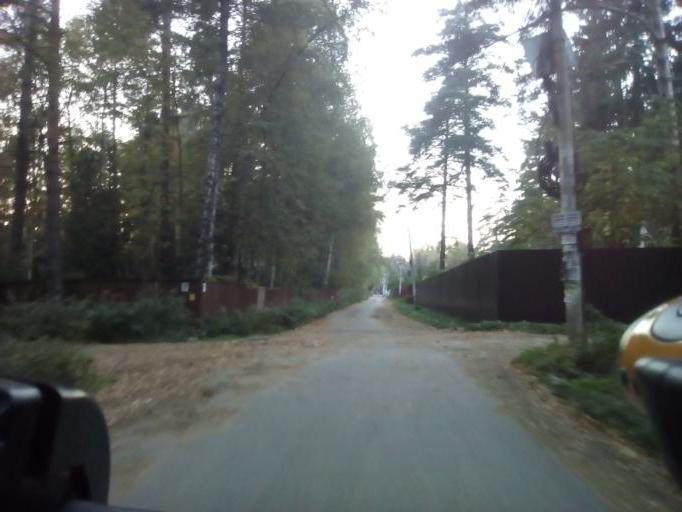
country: RU
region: Moskovskaya
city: Kratovo
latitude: 55.5941
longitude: 38.1971
